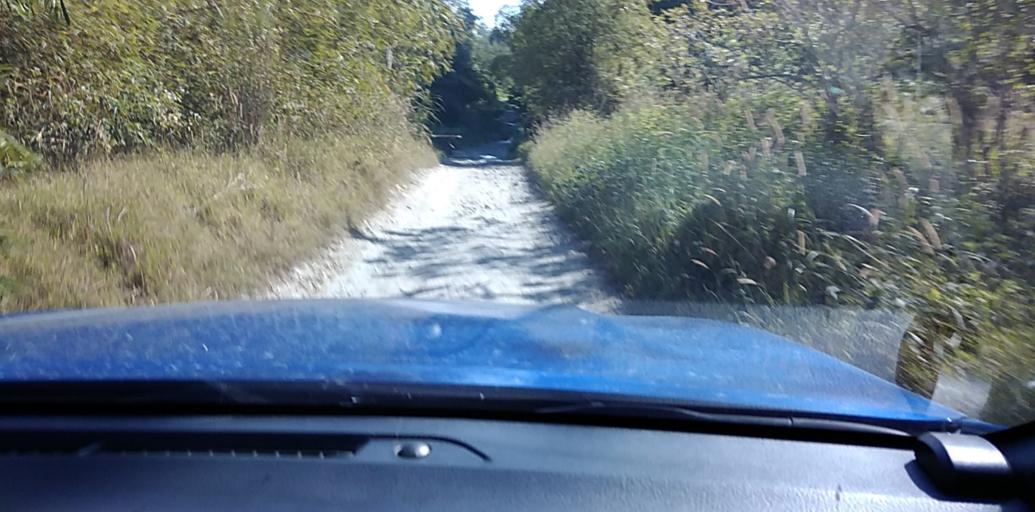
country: PH
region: Central Luzon
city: Santol
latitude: 15.1679
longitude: 120.4866
